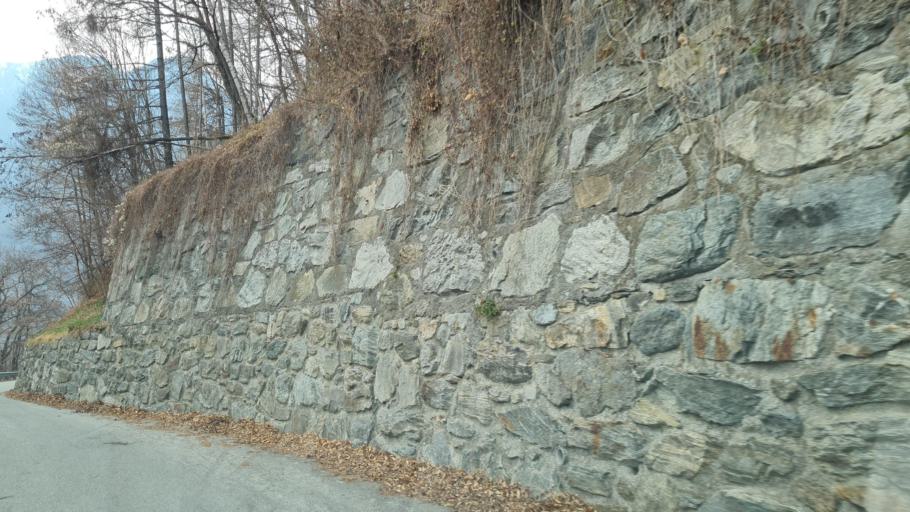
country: IT
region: Aosta Valley
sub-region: Valle d'Aosta
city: Pont-Bozet
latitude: 45.6108
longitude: 7.7005
